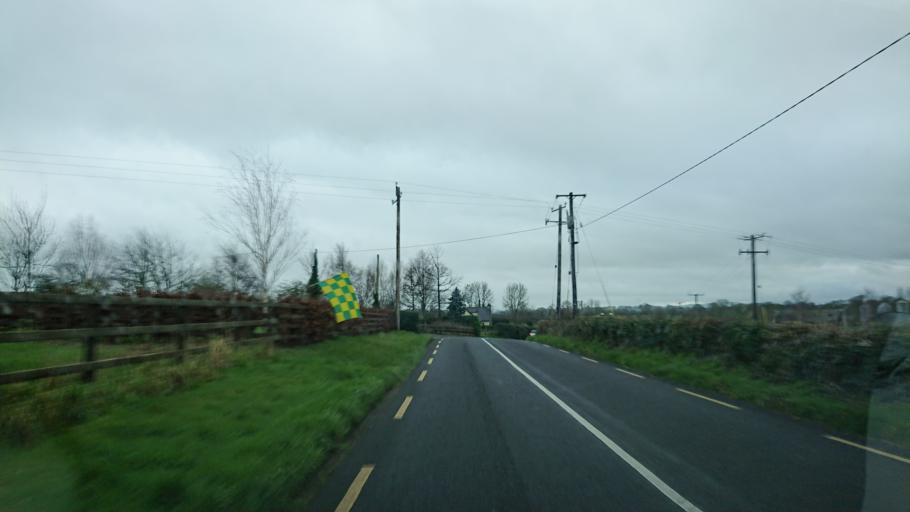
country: IE
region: Leinster
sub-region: Kilkenny
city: Callan
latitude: 52.5394
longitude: -7.2820
